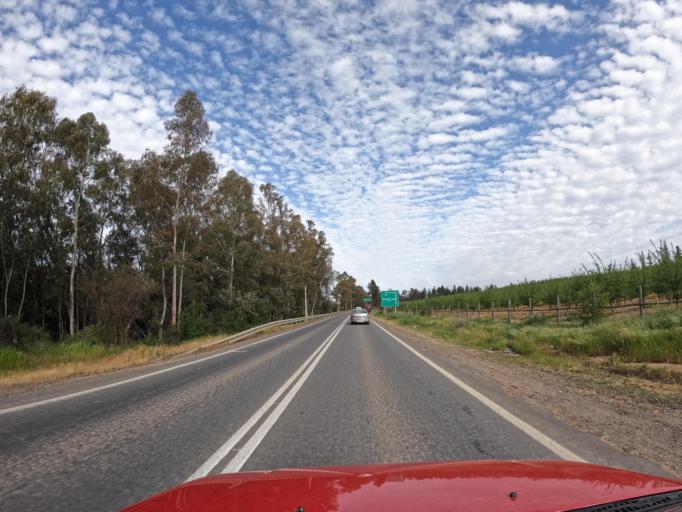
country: CL
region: O'Higgins
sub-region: Provincia de Colchagua
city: Santa Cruz
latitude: -34.3291
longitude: -71.7508
